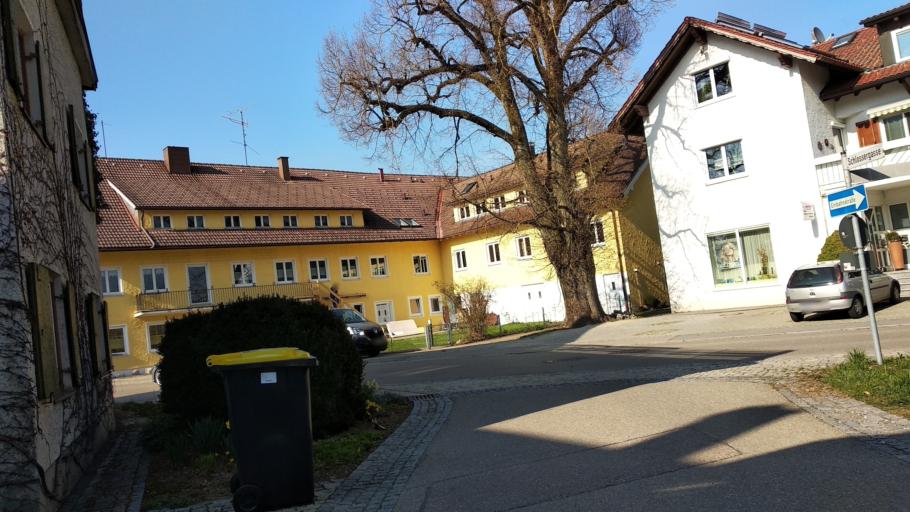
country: DE
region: Bavaria
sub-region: Swabia
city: Legau
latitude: 47.8557
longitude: 10.1311
